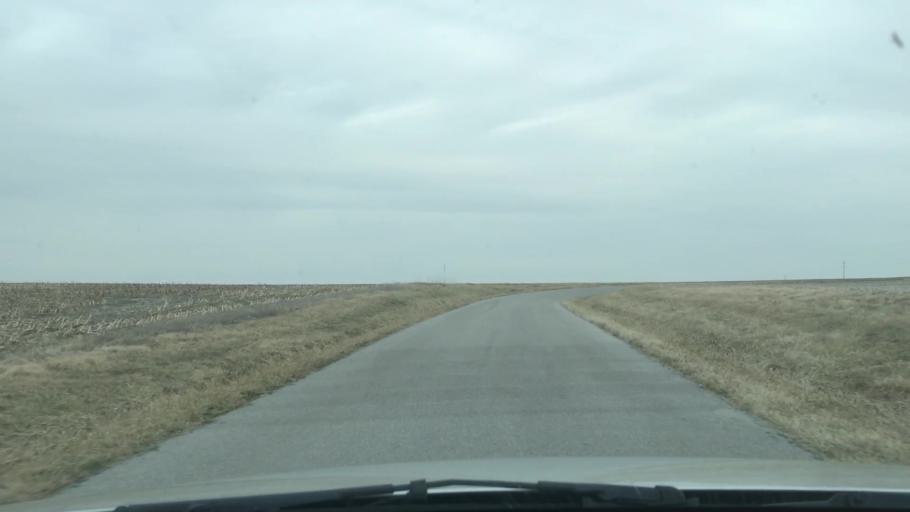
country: US
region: Kentucky
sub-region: Edmonson County
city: Brownsville
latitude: 37.0537
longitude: -86.2403
